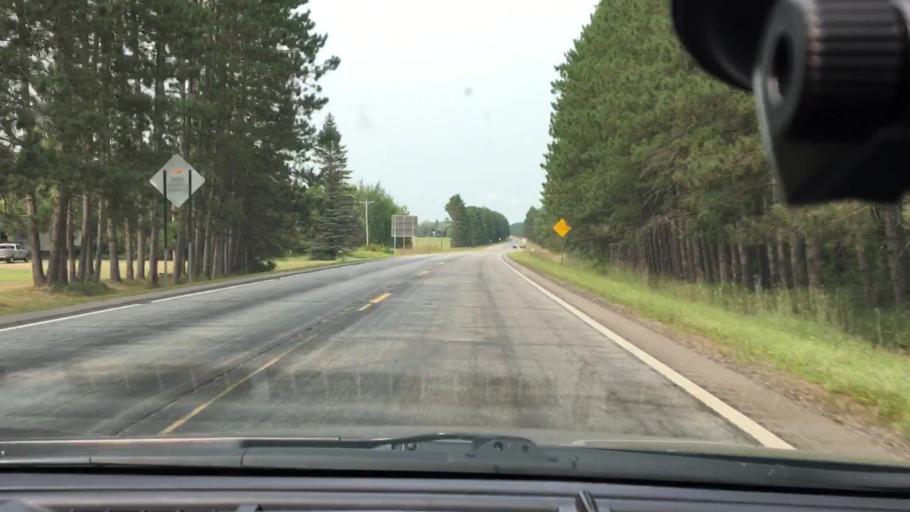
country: US
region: Minnesota
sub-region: Crow Wing County
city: Cross Lake
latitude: 46.7517
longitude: -93.9670
